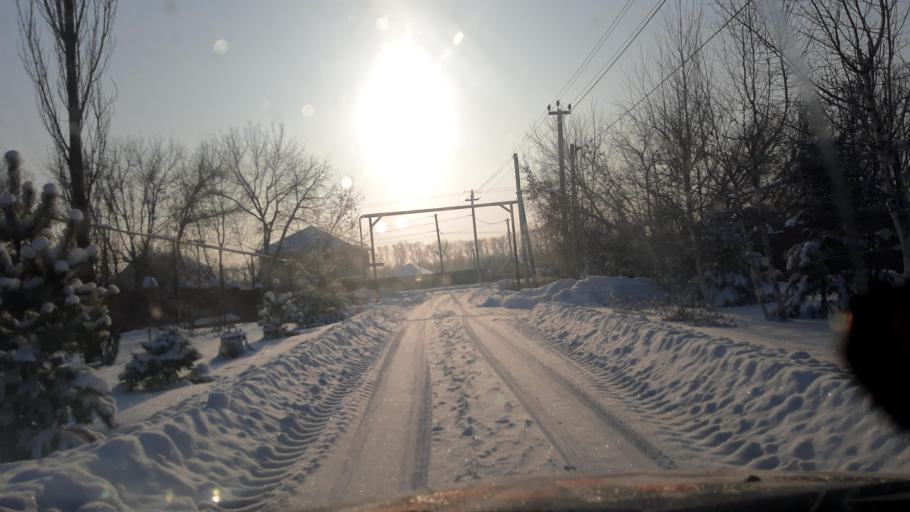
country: RU
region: Bashkortostan
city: Ufa
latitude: 54.5437
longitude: 55.9346
